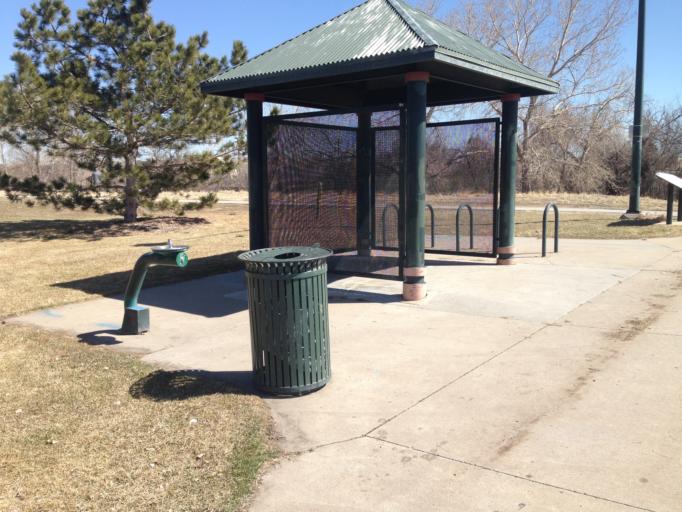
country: US
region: Colorado
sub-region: Adams County
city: Commerce City
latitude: 39.7886
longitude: -104.9734
